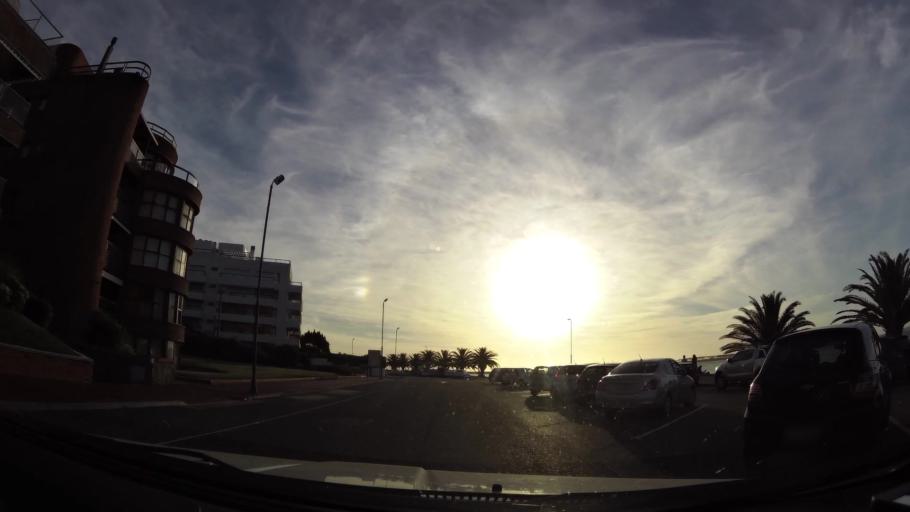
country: UY
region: Maldonado
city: Punta del Este
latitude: -34.9579
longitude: -54.9435
